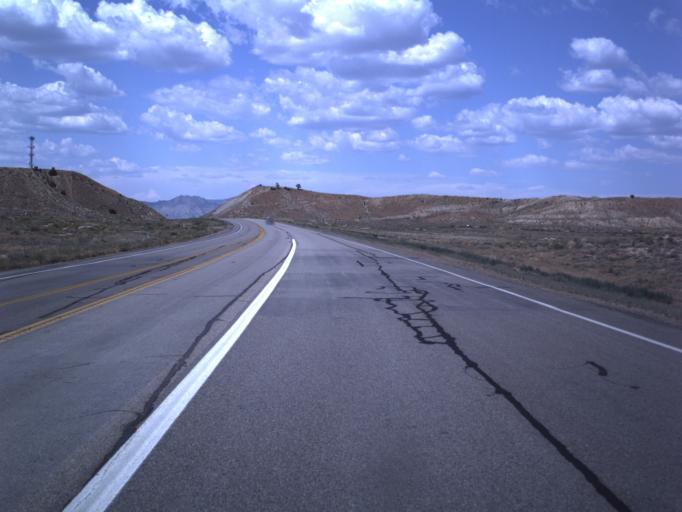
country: US
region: Utah
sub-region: Carbon County
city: Price
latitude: 39.5386
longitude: -110.8148
